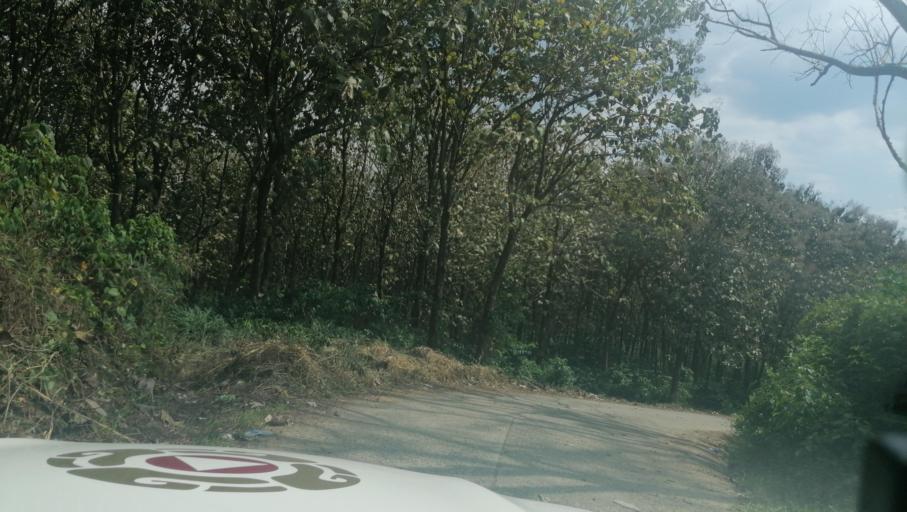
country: MX
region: Chiapas
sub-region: Cacahoatan
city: Benito Juarez
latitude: 15.0304
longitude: -92.2346
